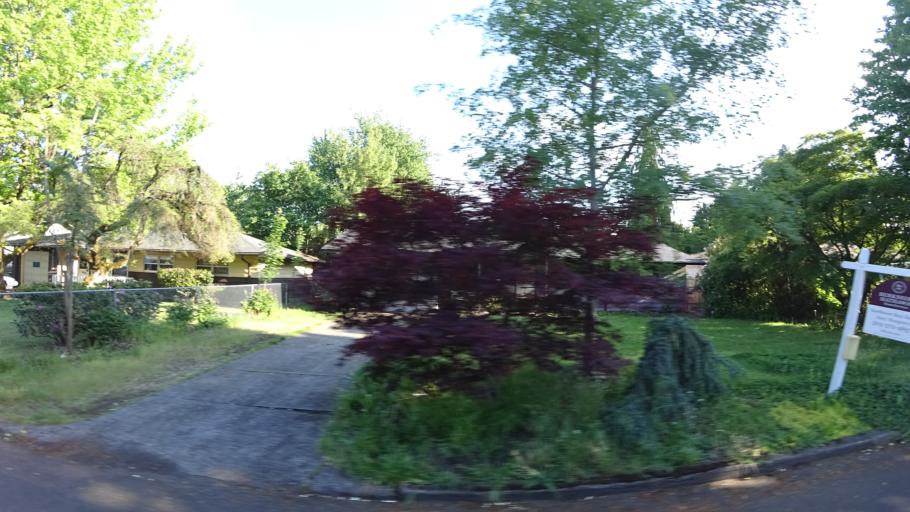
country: US
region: Oregon
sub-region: Multnomah County
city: Gresham
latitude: 45.5105
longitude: -122.4934
